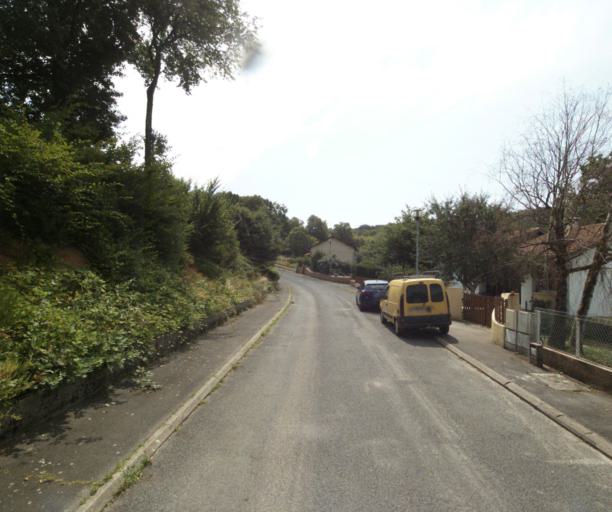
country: FR
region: Bourgogne
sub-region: Departement de Saone-et-Loire
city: Gueugnon
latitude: 46.5925
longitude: 4.0765
